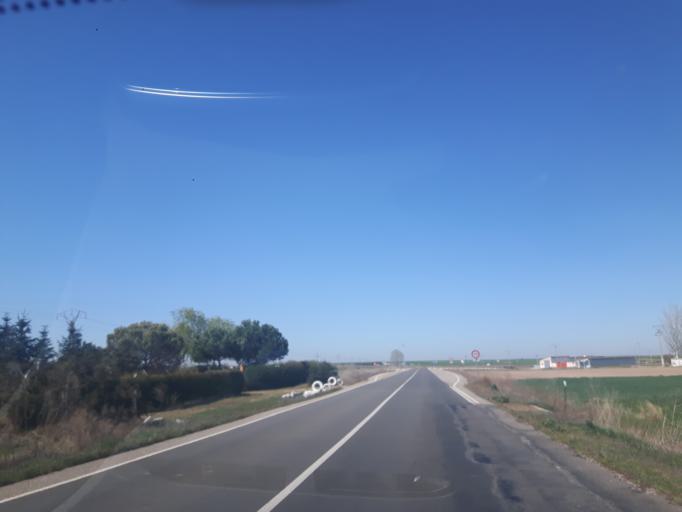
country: ES
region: Castille and Leon
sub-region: Provincia de Salamanca
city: Nava de Sotrobal
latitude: 40.8874
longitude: -5.2844
